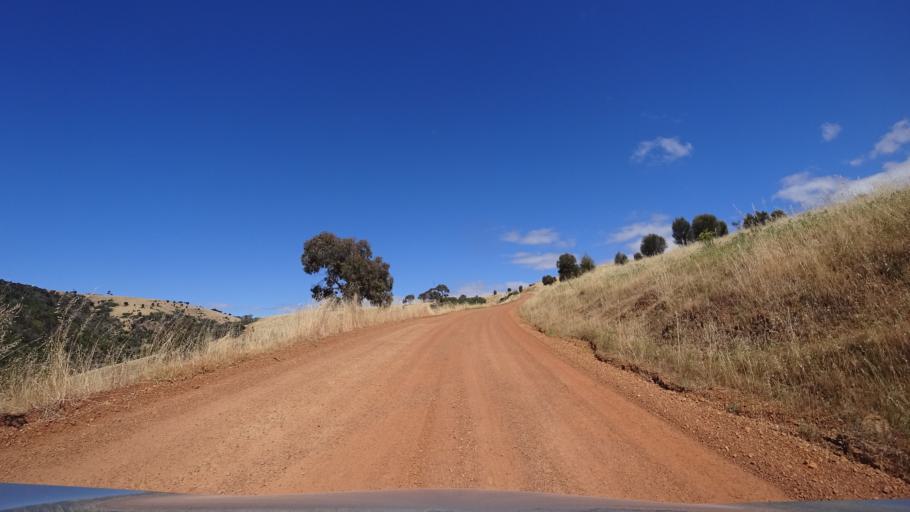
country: AU
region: South Australia
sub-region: Kangaroo Island
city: Kingscote
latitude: -35.6823
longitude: 136.9728
